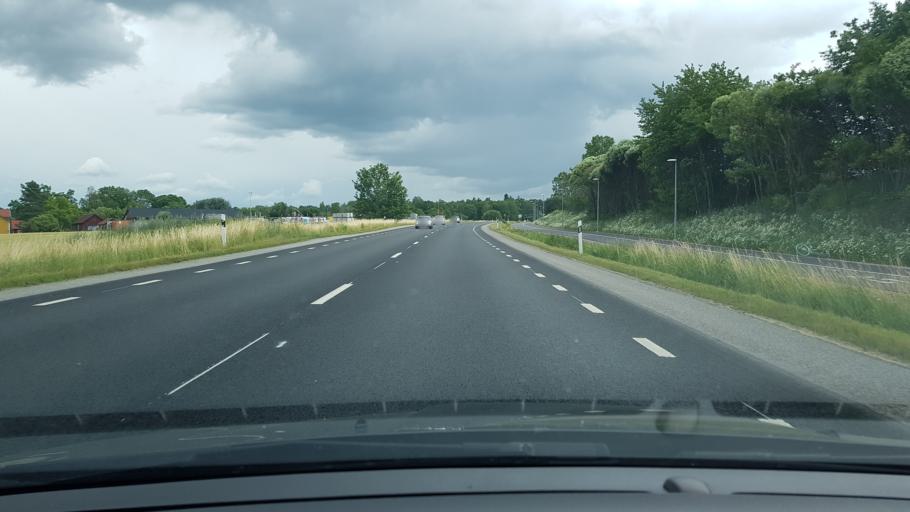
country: SE
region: Uppsala
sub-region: Uppsala Kommun
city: Saevja
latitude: 59.8256
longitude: 17.6969
